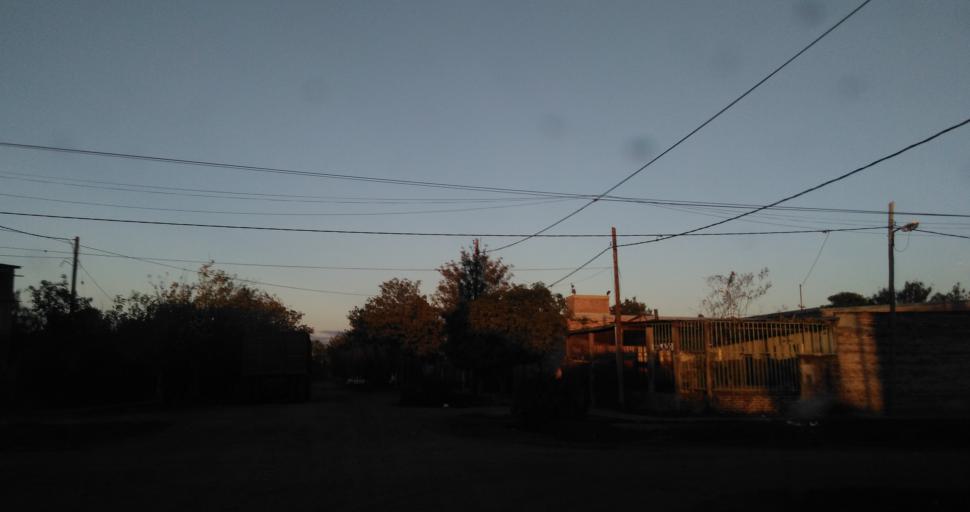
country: AR
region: Chaco
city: Fontana
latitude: -27.4375
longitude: -59.0194
